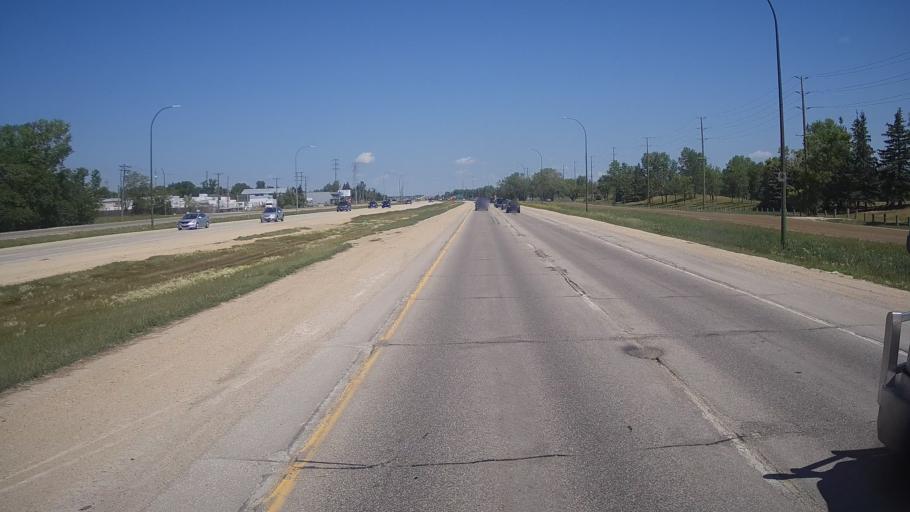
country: CA
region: Manitoba
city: Winnipeg
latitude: 49.9324
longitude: -97.0433
